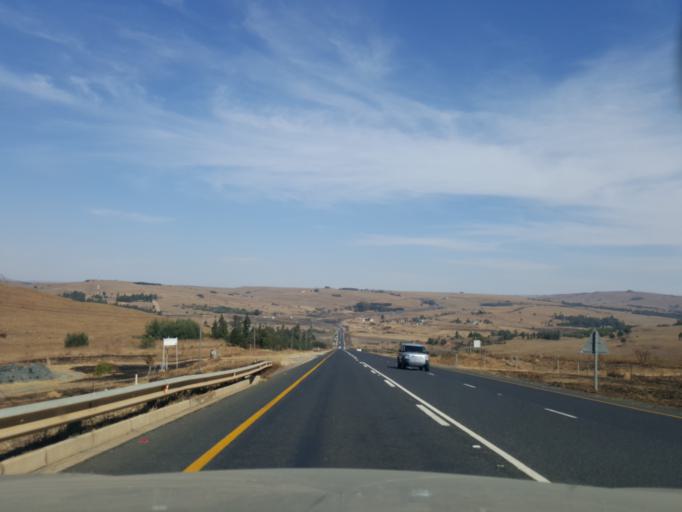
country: ZA
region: Mpumalanga
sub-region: Nkangala District Municipality
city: Belfast
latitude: -25.5976
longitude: 30.2914
